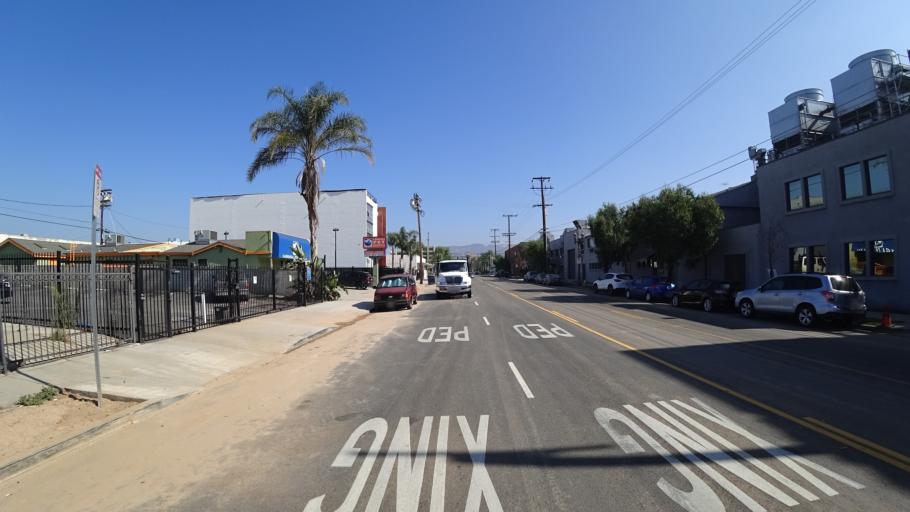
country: US
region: California
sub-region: Los Angeles County
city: Hollywood
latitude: 34.0860
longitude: -118.3288
